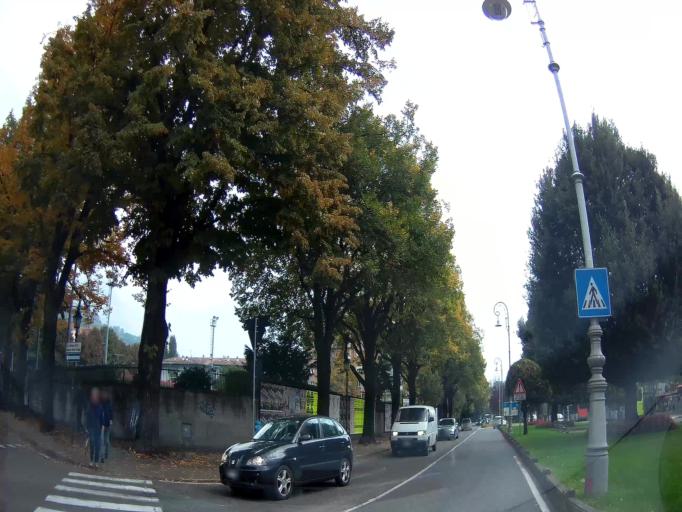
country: IT
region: Trentino-Alto Adige
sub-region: Bolzano
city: Merano
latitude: 46.6736
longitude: 11.1496
